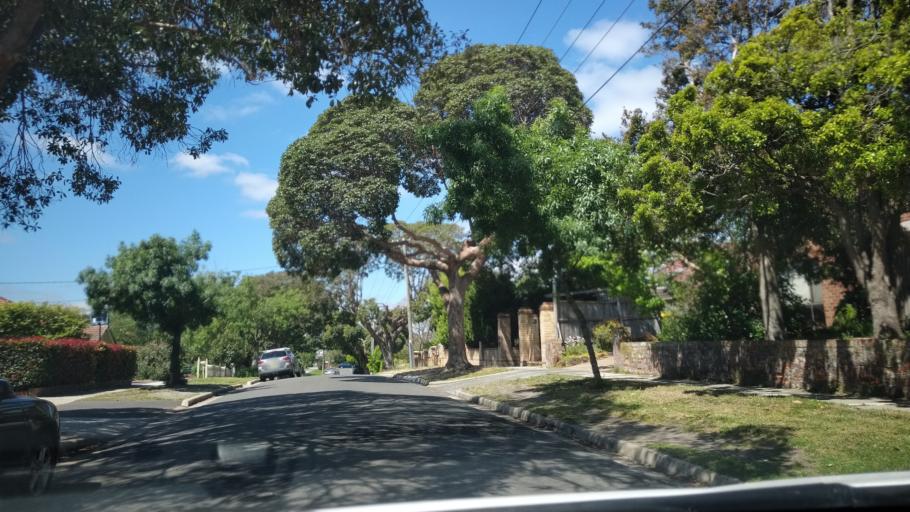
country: AU
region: Victoria
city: Hughesdale
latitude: -37.9034
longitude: 145.0762
